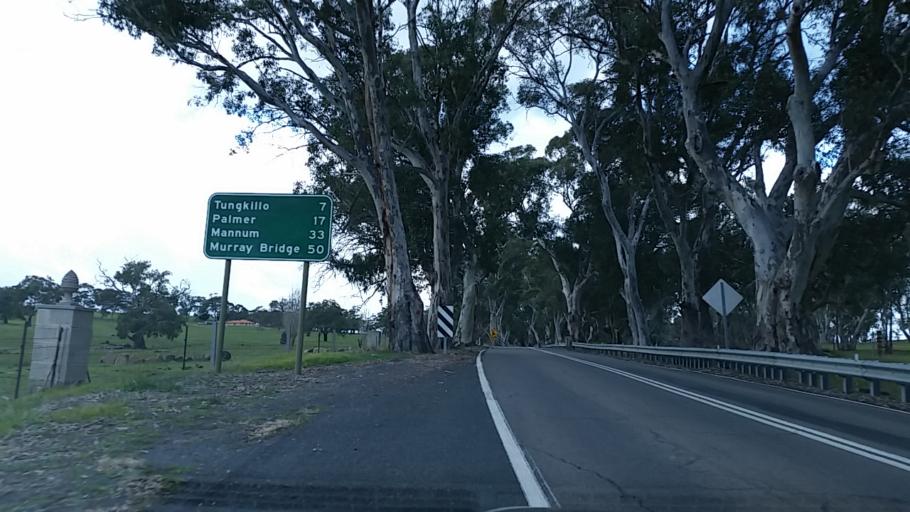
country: AU
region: South Australia
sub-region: Adelaide Hills
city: Birdwood
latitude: -34.8004
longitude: 139.0058
